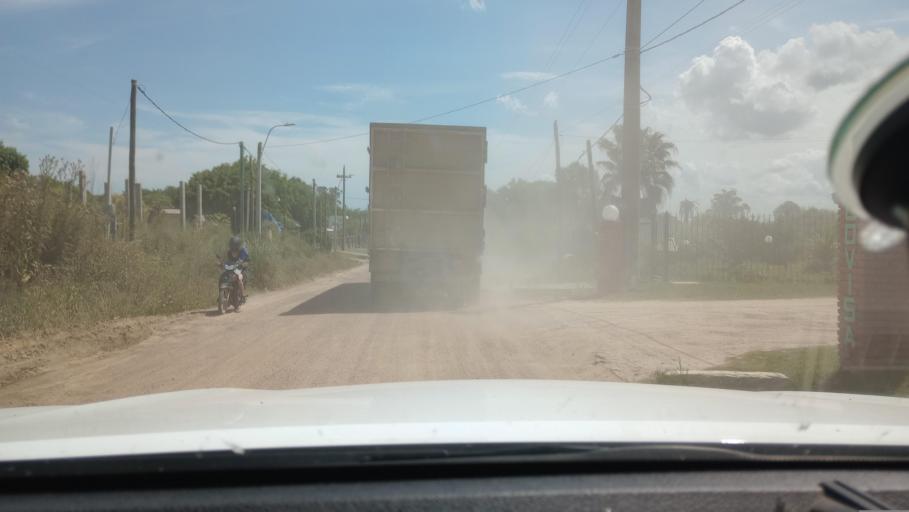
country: UY
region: Canelones
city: Sauce
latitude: -34.6595
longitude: -56.0579
